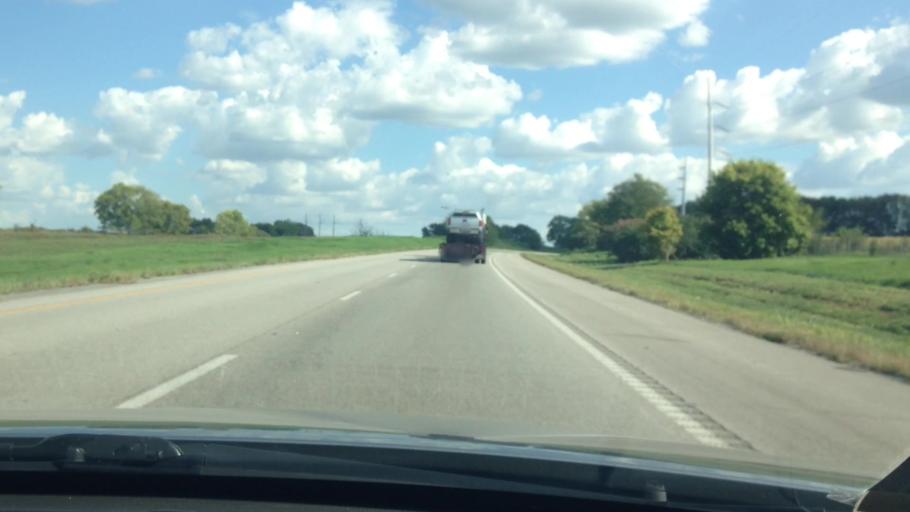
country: US
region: Missouri
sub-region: Clay County
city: Pleasant Valley
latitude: 39.3087
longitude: -94.5148
